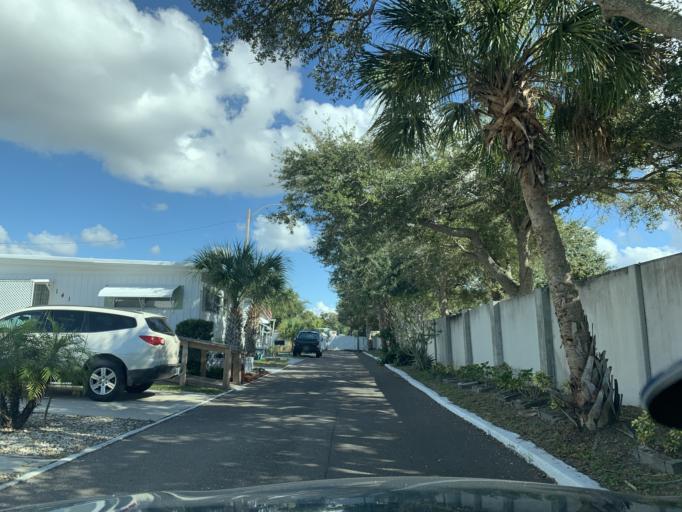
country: US
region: Florida
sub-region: Pinellas County
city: Bay Pines
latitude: 27.8101
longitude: -82.7505
